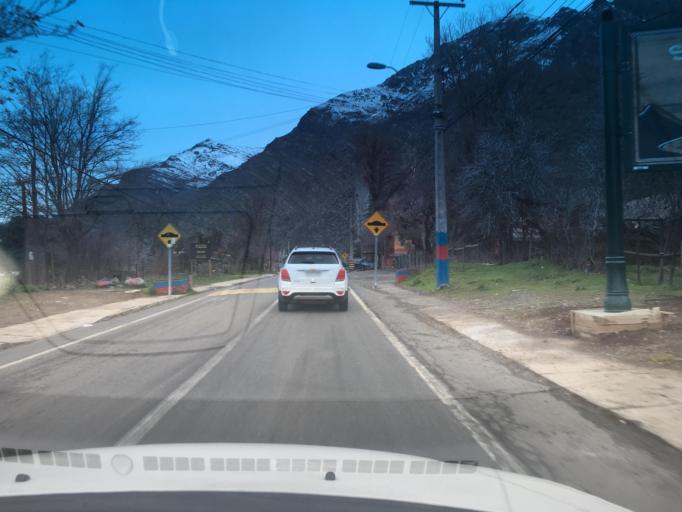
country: CL
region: Santiago Metropolitan
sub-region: Provincia de Cordillera
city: Puente Alto
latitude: -33.7164
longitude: -70.3312
